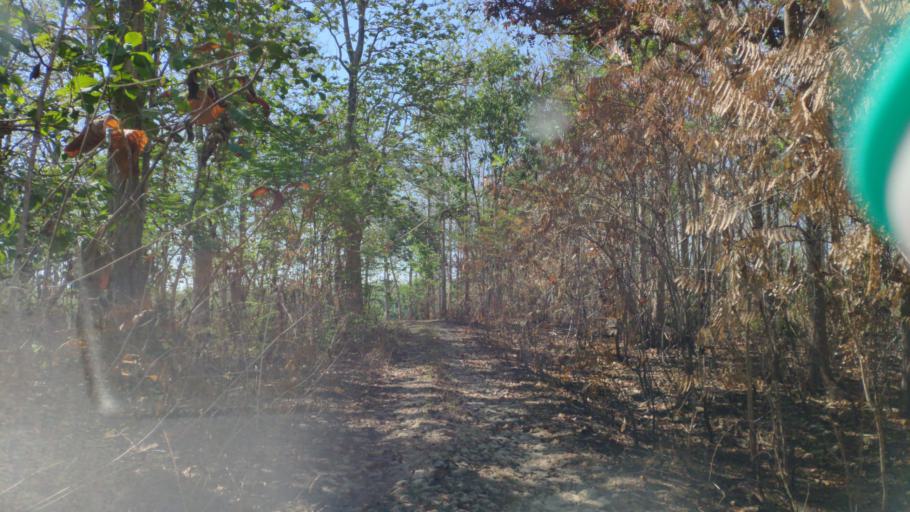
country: ID
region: Central Java
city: Botoh
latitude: -7.0824
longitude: 111.4498
